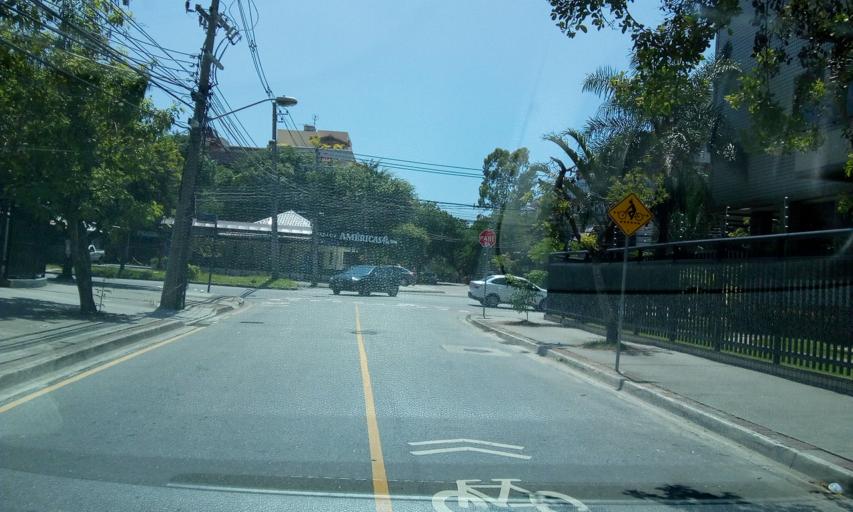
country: BR
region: Rio de Janeiro
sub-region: Nilopolis
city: Nilopolis
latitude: -23.0208
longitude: -43.4593
